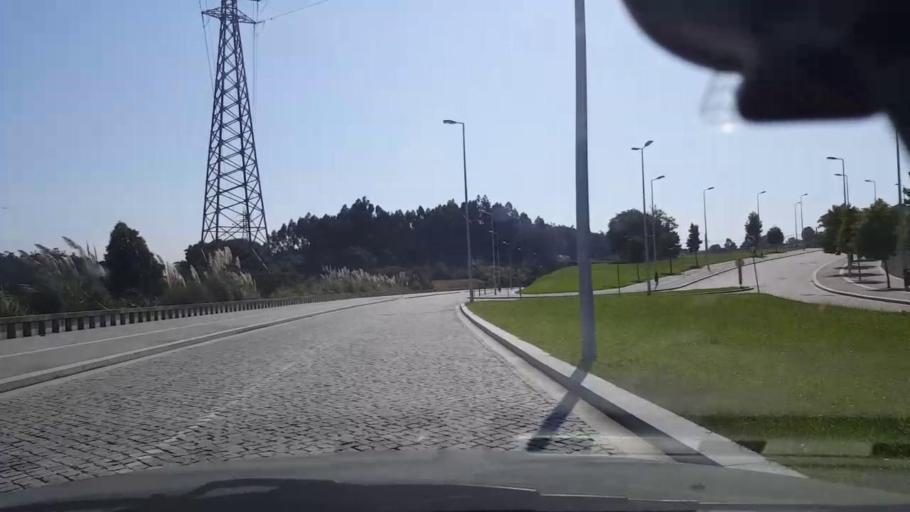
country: PT
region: Porto
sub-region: Vila do Conde
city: Vila do Conde
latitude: 41.3546
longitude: -8.7308
